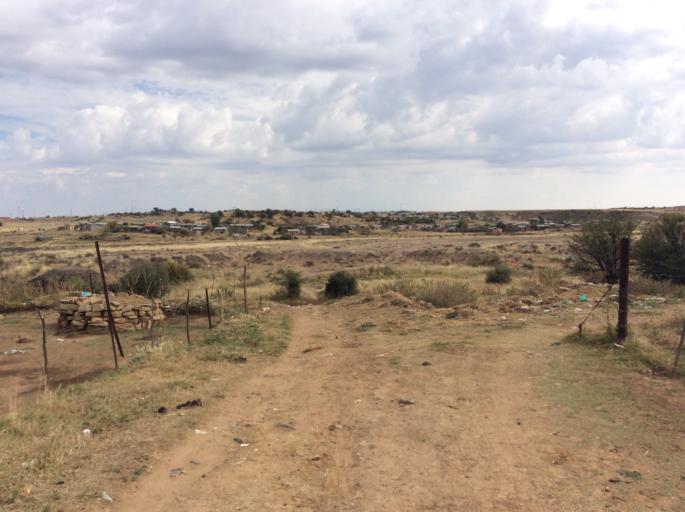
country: LS
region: Mafeteng
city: Mafeteng
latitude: -29.7215
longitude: 27.0244
